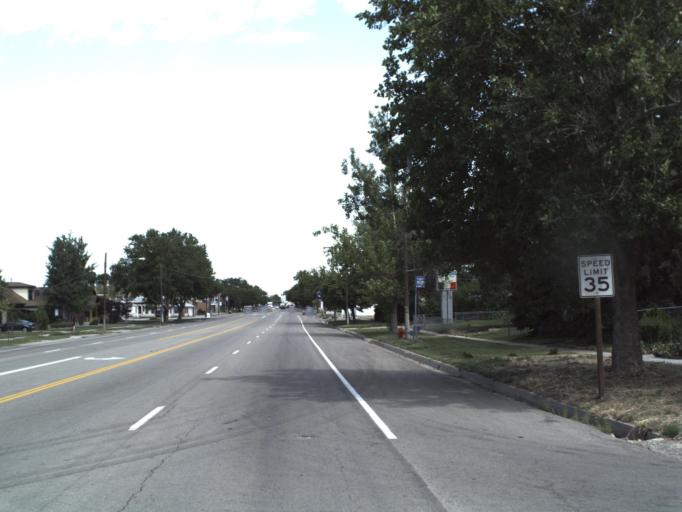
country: US
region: Utah
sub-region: Tooele County
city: Tooele
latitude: 40.5237
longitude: -112.2986
